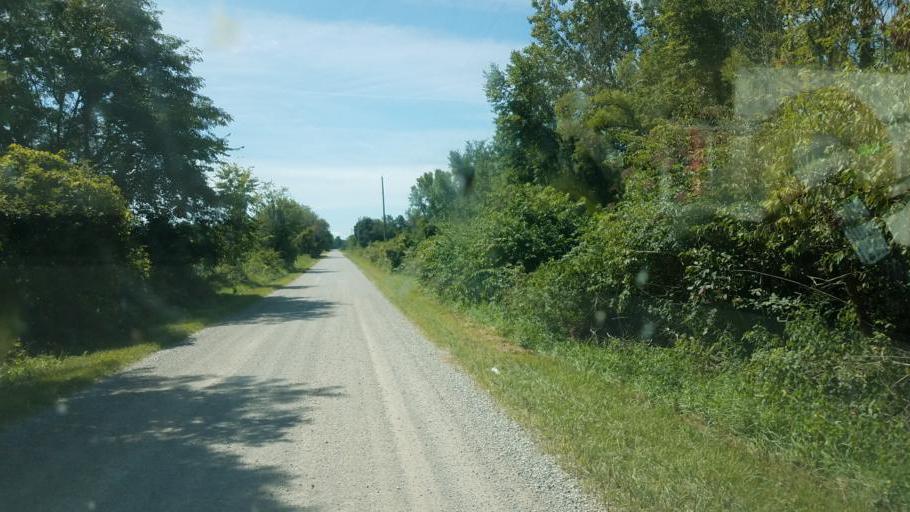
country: US
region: Ohio
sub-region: Morrow County
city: Mount Gilead
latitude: 40.4492
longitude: -82.7265
